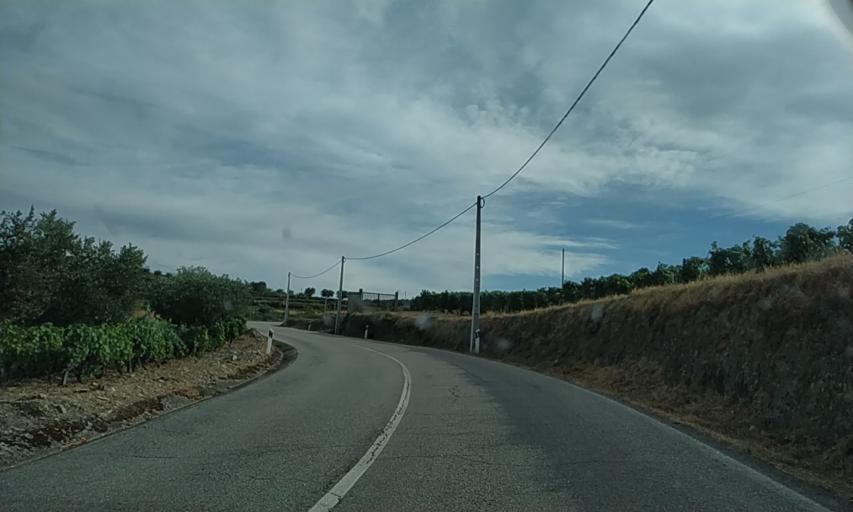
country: PT
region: Viseu
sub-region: Sao Joao da Pesqueira
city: Sao Joao da Pesqueira
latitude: 41.0774
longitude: -7.3903
